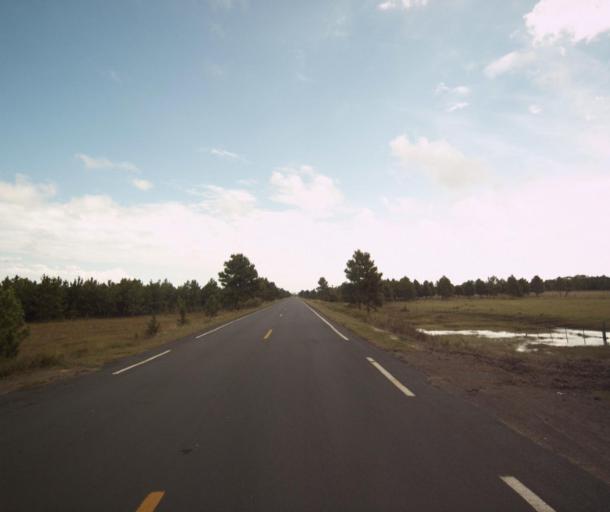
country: BR
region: Rio Grande do Sul
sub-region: Tapes
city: Tapes
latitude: -31.4315
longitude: -51.1899
